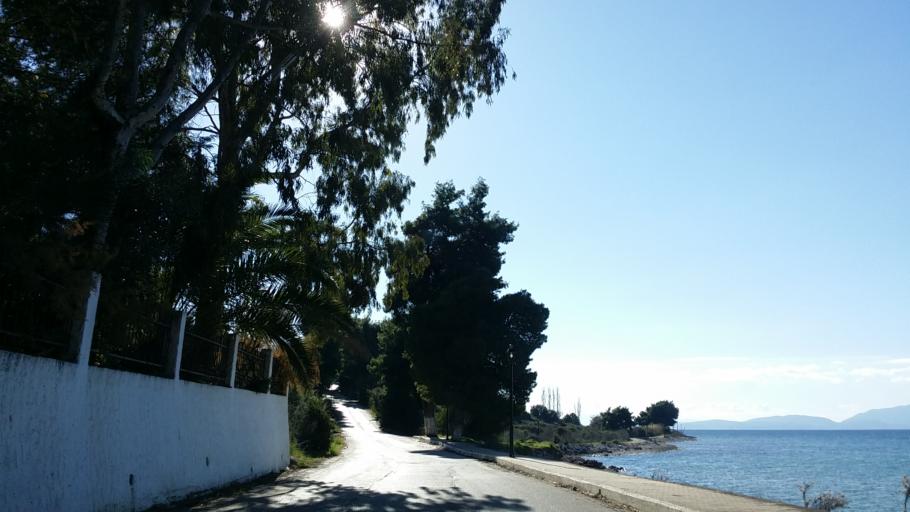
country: GR
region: West Greece
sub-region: Nomos Aitolias kai Akarnanias
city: Palairos
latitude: 38.7763
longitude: 20.8812
